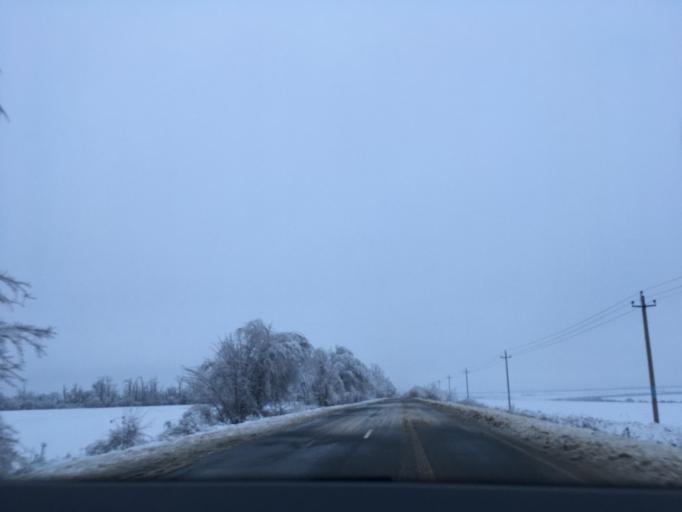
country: RU
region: Voronezj
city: Verkhniy Mamon
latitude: 50.0232
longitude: 40.0818
